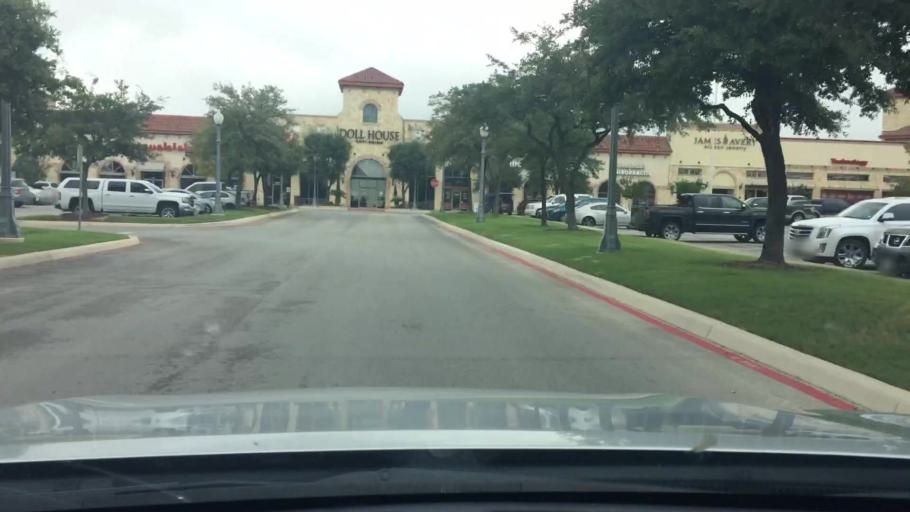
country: US
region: Texas
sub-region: Bexar County
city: Hollywood Park
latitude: 29.6099
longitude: -98.5110
